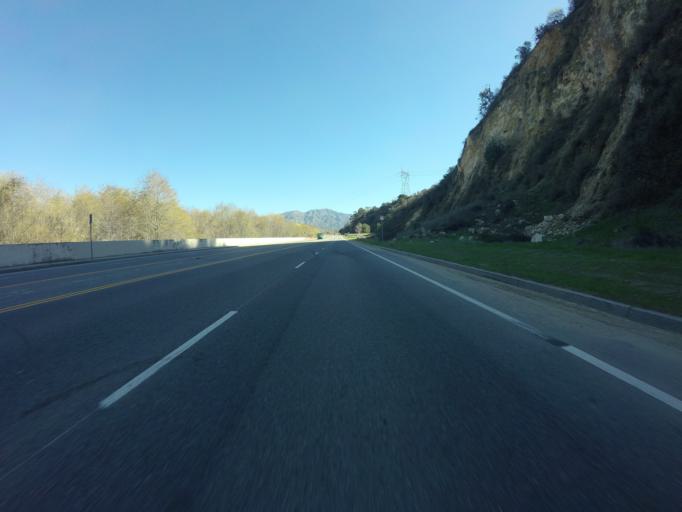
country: US
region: California
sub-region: Los Angeles County
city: San Fernando
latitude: 34.2662
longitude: -118.3626
